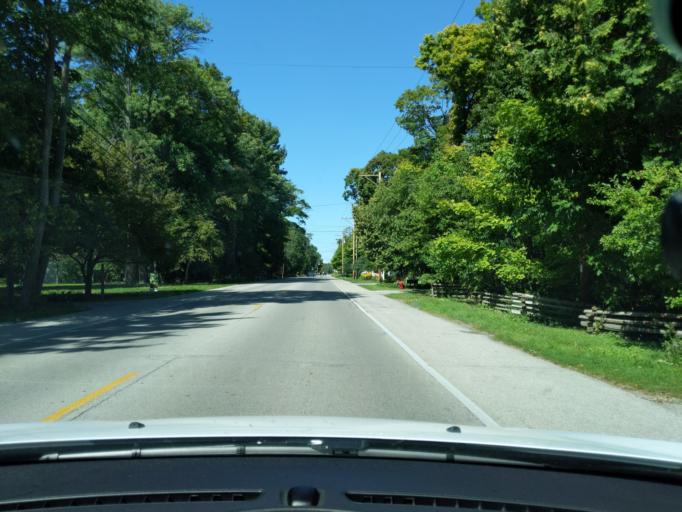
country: US
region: Wisconsin
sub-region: Door County
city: Sturgeon Bay
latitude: 45.1969
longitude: -87.1189
